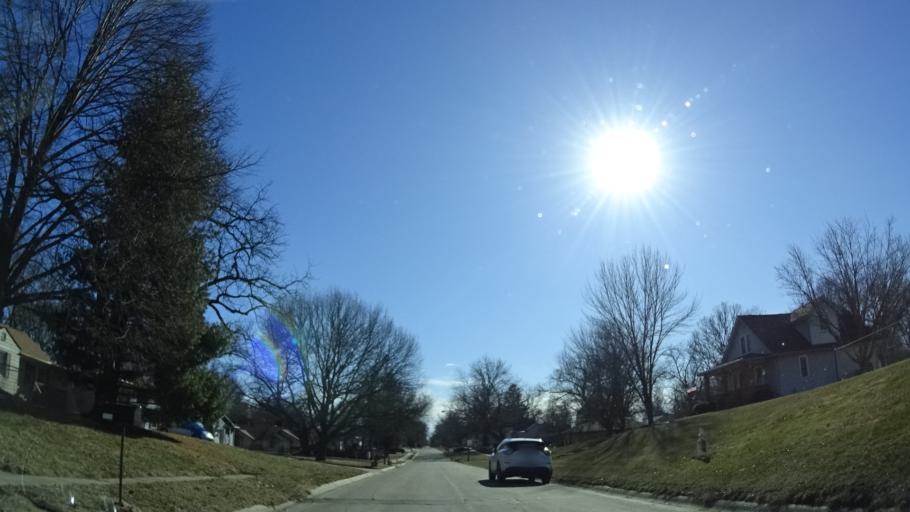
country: US
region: Nebraska
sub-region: Sarpy County
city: Bellevue
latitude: 41.1434
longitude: -95.8909
